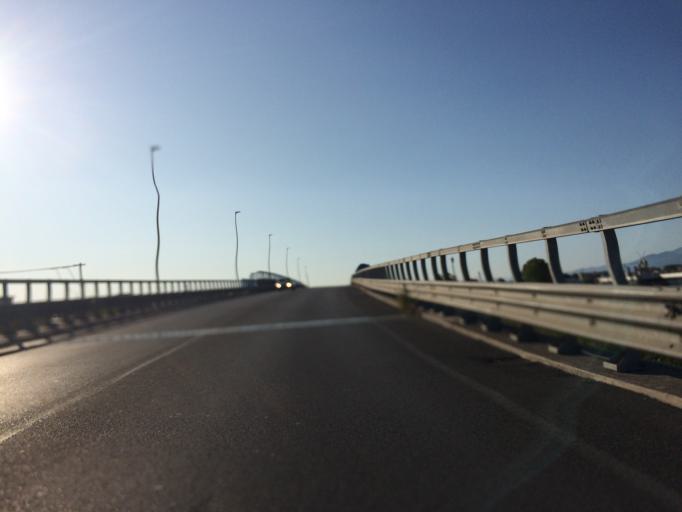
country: IT
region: Tuscany
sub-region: Provincia di Lucca
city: Viareggio
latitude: 43.8611
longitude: 10.2627
